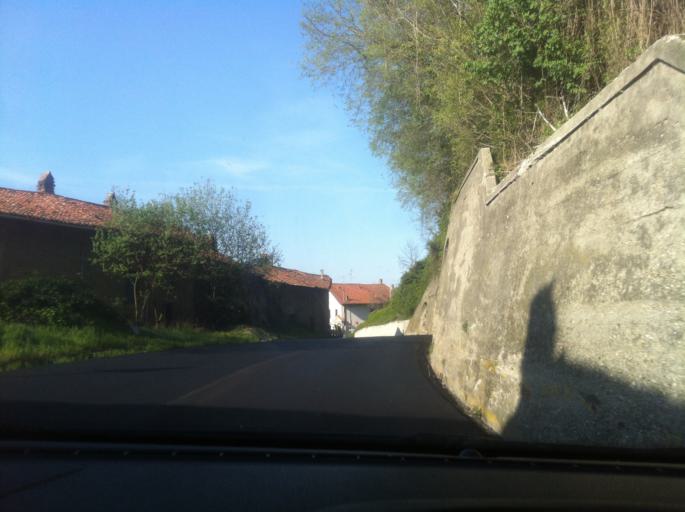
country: IT
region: Piedmont
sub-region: Provincia di Torino
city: Candia Canavese
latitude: 45.3295
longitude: 7.8838
